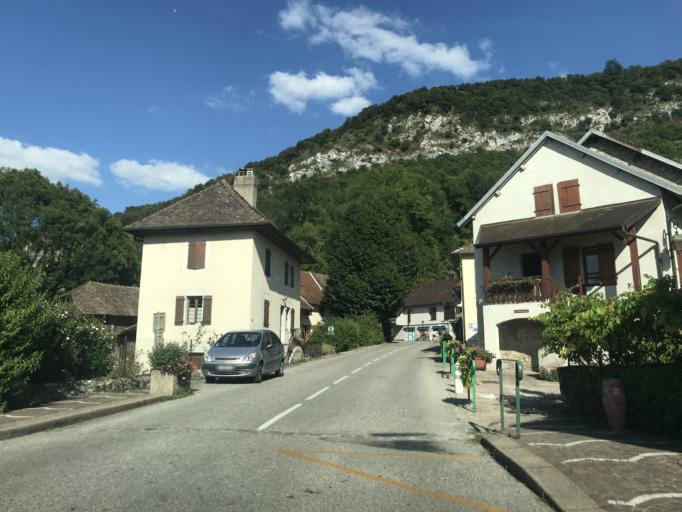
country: FR
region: Rhone-Alpes
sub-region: Departement de l'Ain
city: Culoz
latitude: 45.8091
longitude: 5.7929
